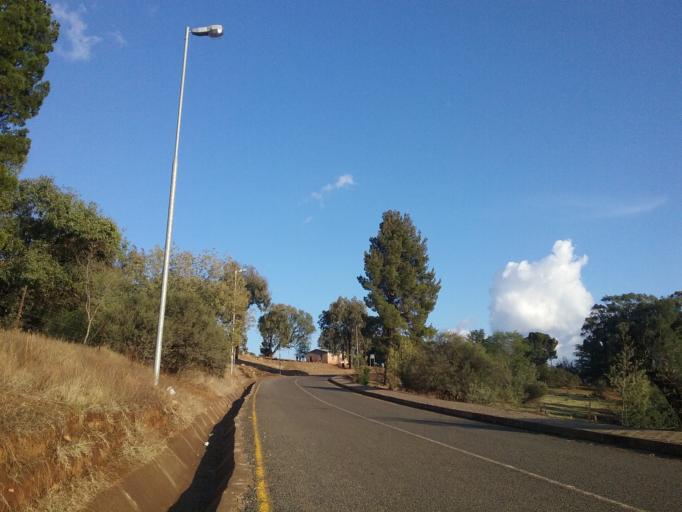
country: LS
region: Quthing
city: Quthing
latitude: -30.4104
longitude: 27.7087
